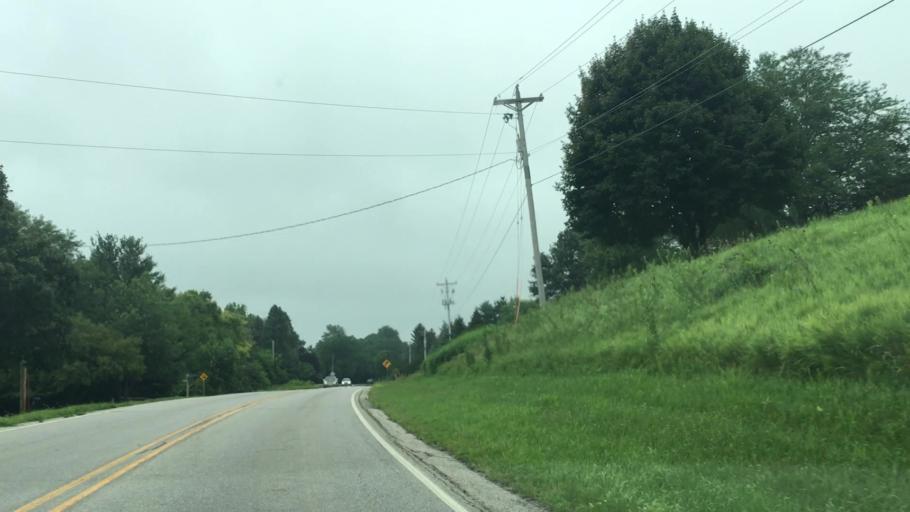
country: US
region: Iowa
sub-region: Johnson County
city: North Liberty
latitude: 41.7212
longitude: -91.5580
